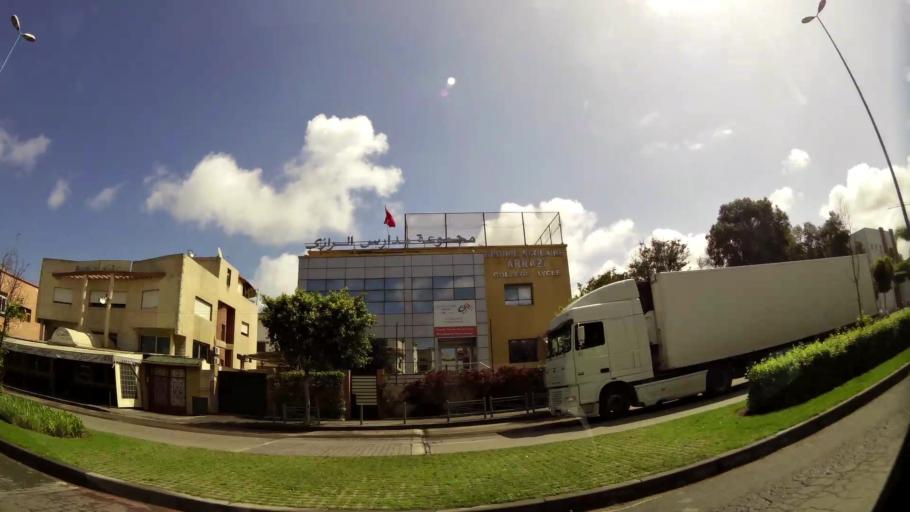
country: MA
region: Grand Casablanca
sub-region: Mediouna
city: Tit Mellil
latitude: 33.6137
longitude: -7.5312
